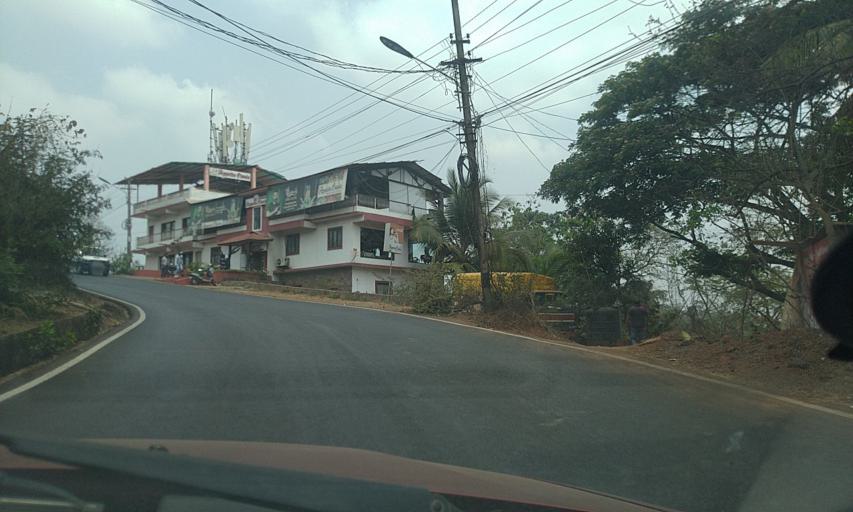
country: IN
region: Goa
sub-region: North Goa
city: Mapuca
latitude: 15.6005
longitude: 73.8085
